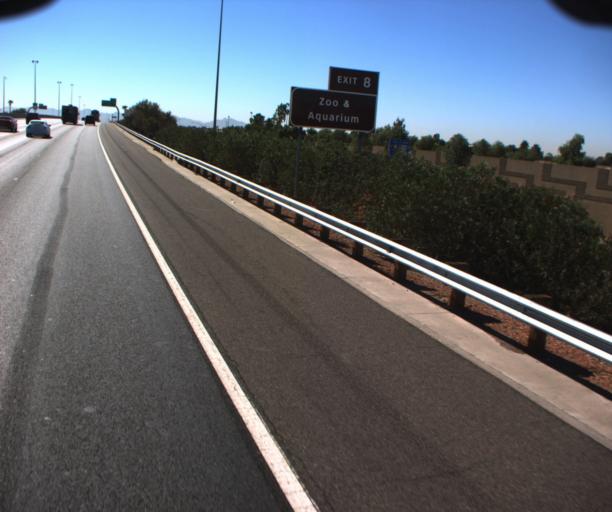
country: US
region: Arizona
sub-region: Maricopa County
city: Peoria
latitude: 33.5692
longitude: -112.2574
